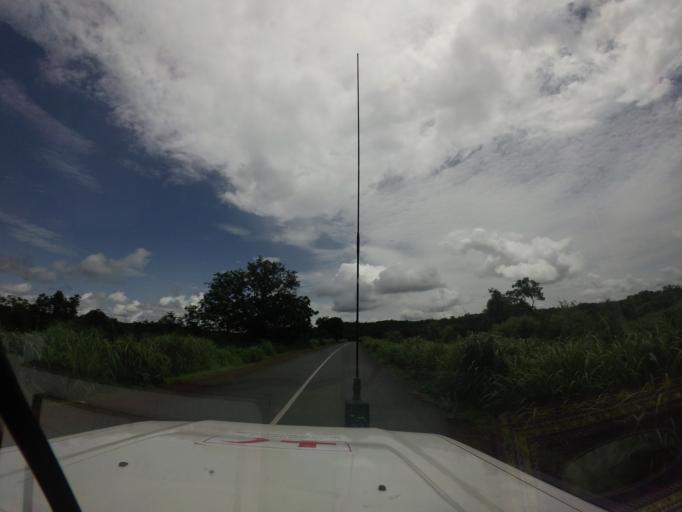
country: GN
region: Faranah
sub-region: Faranah Prefecture
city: Faranah
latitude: 10.0140
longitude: -10.9341
